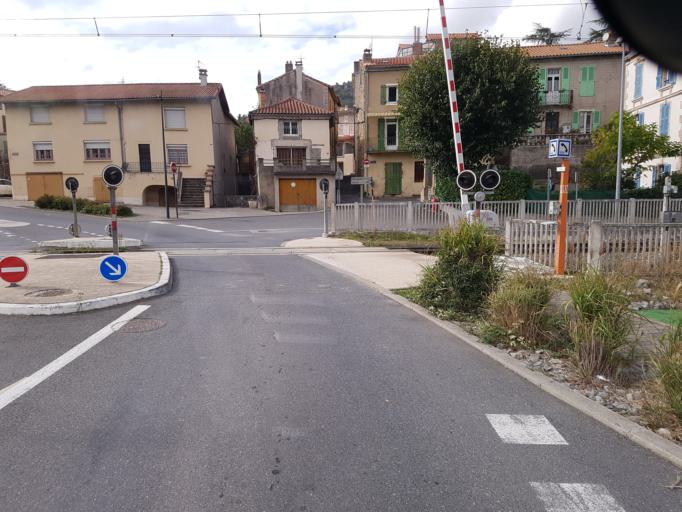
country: FR
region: Midi-Pyrenees
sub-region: Departement de l'Aveyron
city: Saint-Georges-de-Luzencon
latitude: 44.0639
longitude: 2.9840
